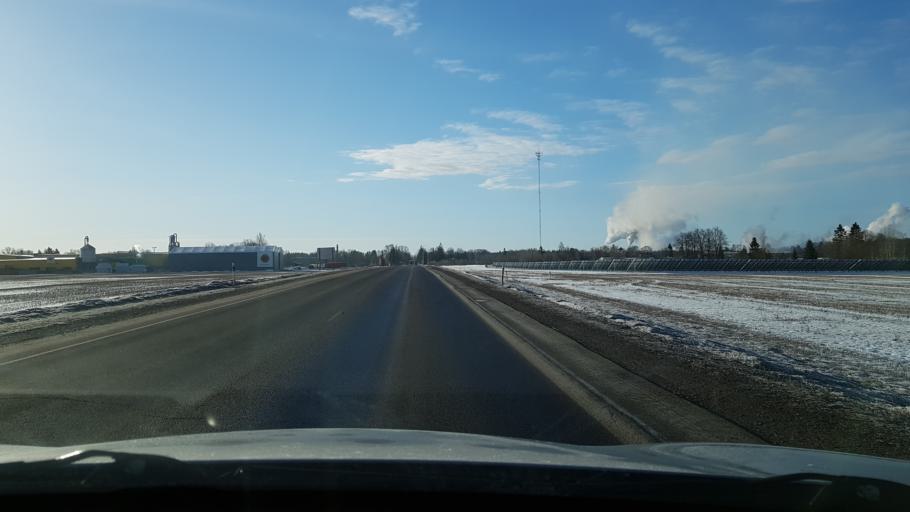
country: EE
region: Jogevamaa
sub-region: Poltsamaa linn
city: Poltsamaa
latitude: 58.7428
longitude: 25.7690
